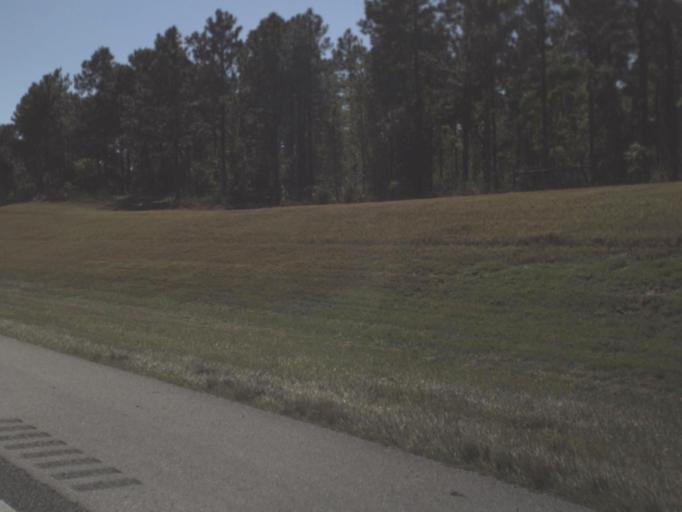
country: US
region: Florida
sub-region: Lake County
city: Minneola
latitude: 28.6007
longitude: -81.7204
